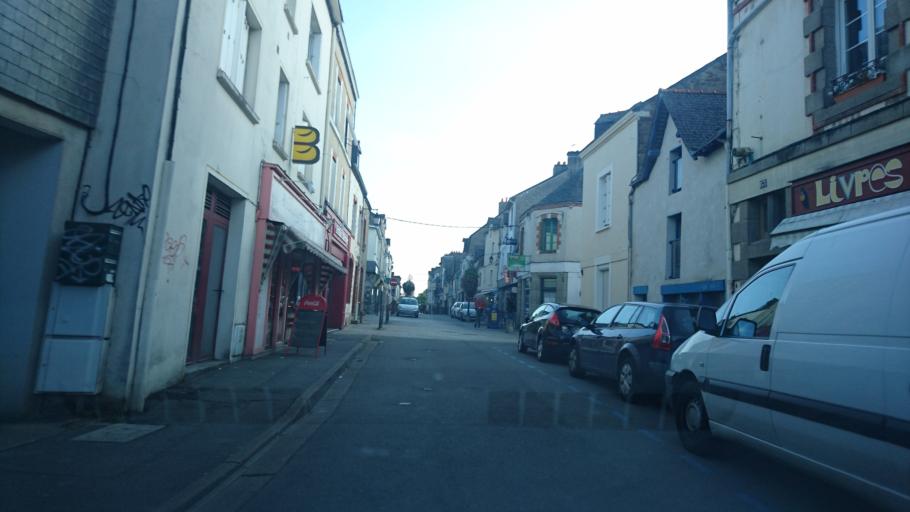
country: FR
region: Brittany
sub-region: Departement d'Ille-et-Vilaine
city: Redon
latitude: 47.6534
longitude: -2.0840
